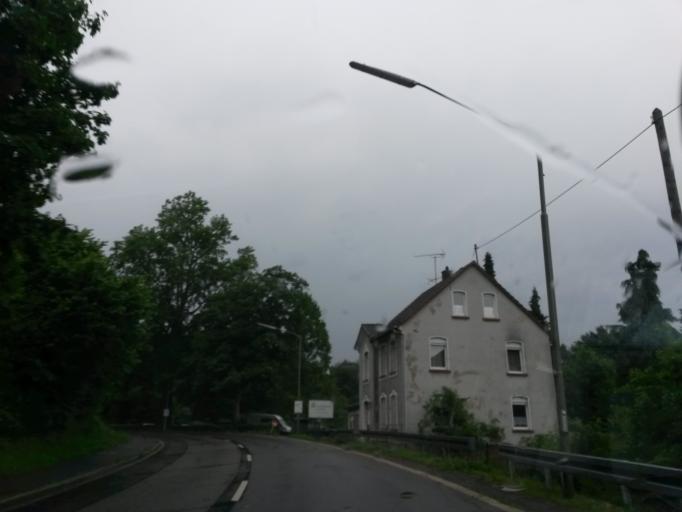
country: DE
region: North Rhine-Westphalia
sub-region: Regierungsbezirk Koln
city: Gummersbach
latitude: 51.0392
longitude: 7.5572
